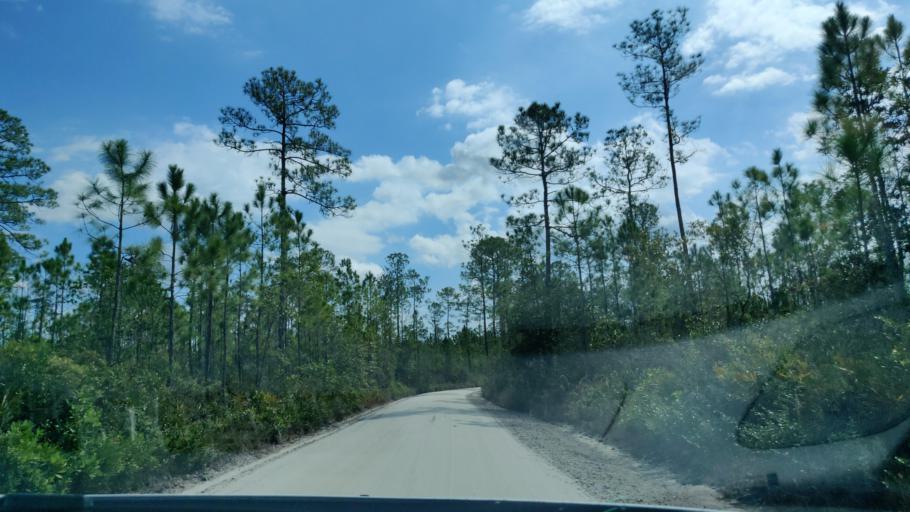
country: US
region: Florida
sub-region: Duval County
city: Baldwin
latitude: 30.1708
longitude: -81.9530
